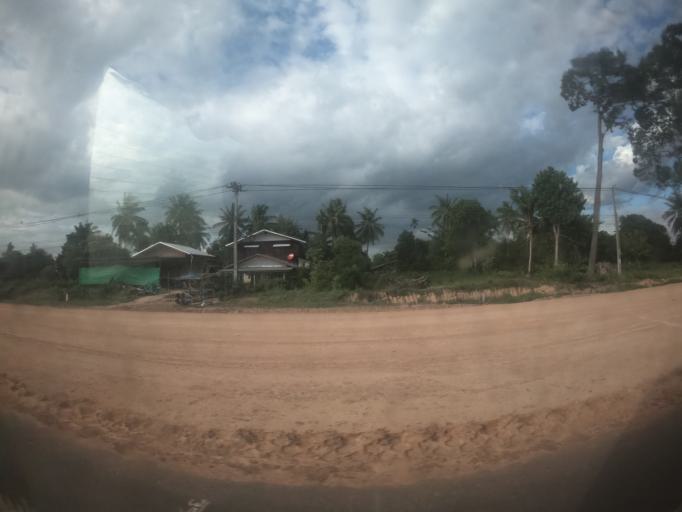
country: TH
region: Surin
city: Kap Choeng
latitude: 14.4908
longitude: 103.5739
